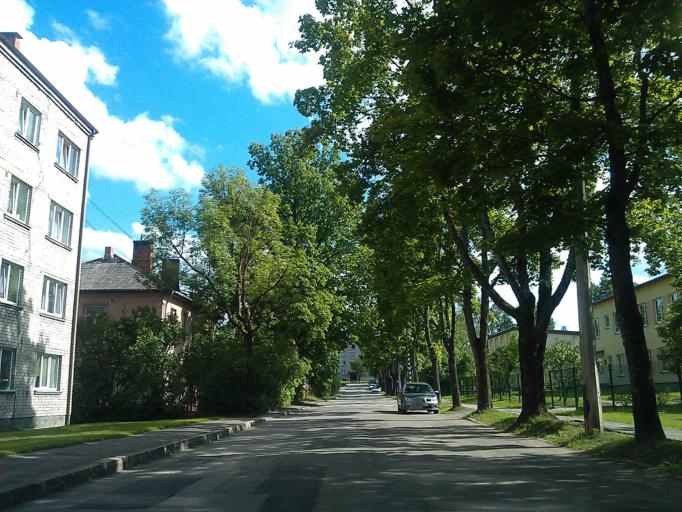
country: LV
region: Cesu Rajons
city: Cesis
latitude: 57.3059
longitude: 25.2685
